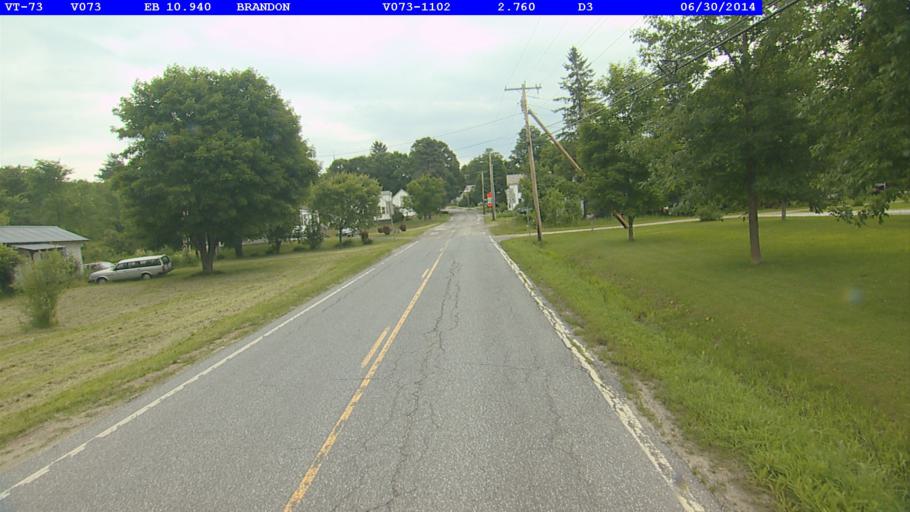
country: US
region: Vermont
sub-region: Rutland County
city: Brandon
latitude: 43.8001
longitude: -73.0989
